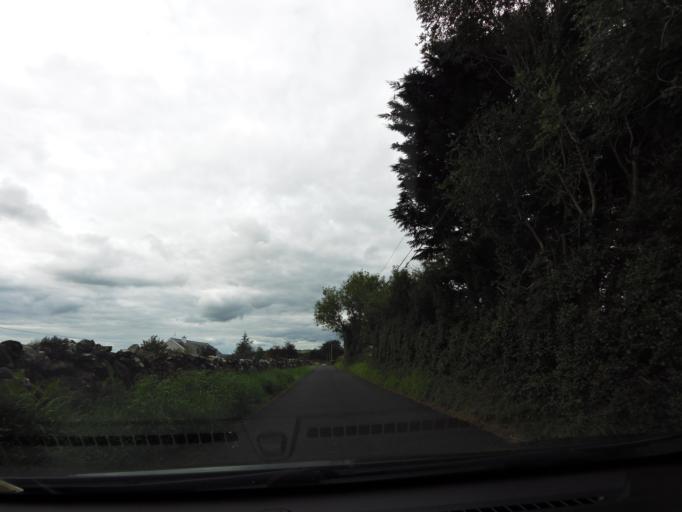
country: IE
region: Connaught
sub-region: County Galway
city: Loughrea
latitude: 53.1475
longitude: -8.4191
